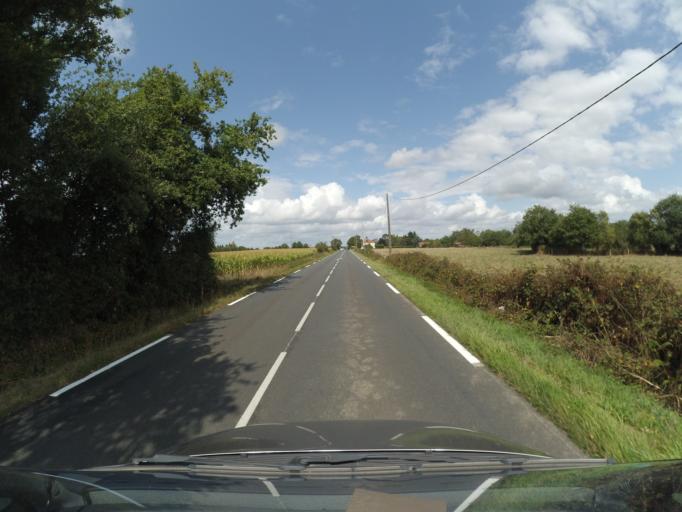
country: FR
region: Pays de la Loire
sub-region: Departement de la Vendee
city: La Bernardiere
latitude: 47.0208
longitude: -1.2711
